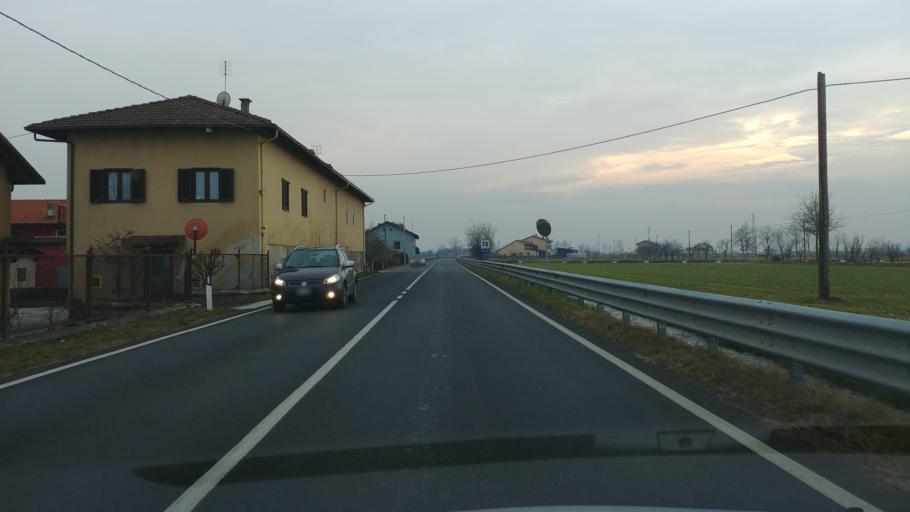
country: IT
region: Piedmont
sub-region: Provincia di Cuneo
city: Montanera
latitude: 44.4759
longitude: 7.6432
